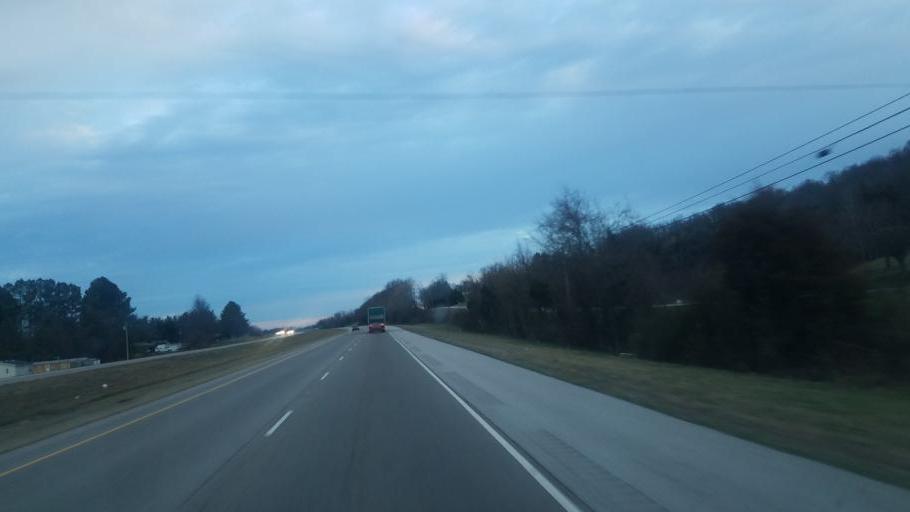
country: US
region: Tennessee
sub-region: White County
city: Sparta
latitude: 36.0051
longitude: -85.5038
